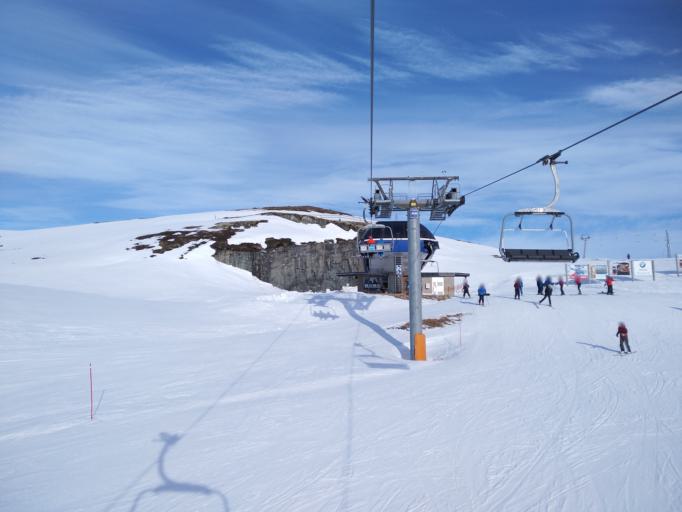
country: NO
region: Aust-Agder
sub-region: Bykle
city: Hovden
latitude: 59.5781
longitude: 7.3211
